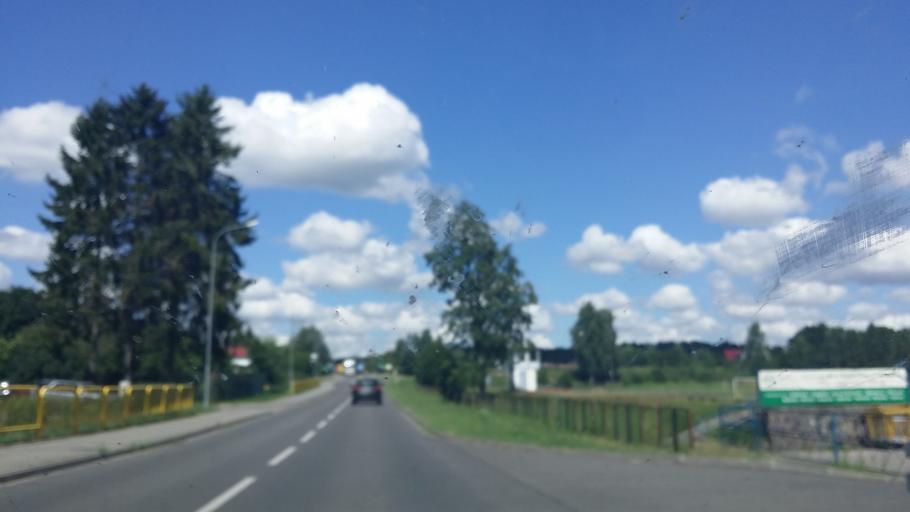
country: PL
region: West Pomeranian Voivodeship
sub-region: Powiat swidwinski
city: Slawoborze
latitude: 53.8946
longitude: 15.7085
